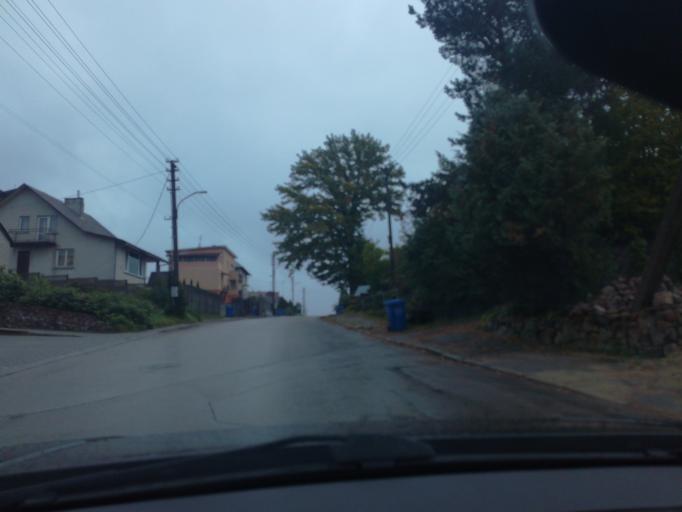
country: LT
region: Alytaus apskritis
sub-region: Alytus
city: Alytus
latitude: 54.4005
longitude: 24.0717
